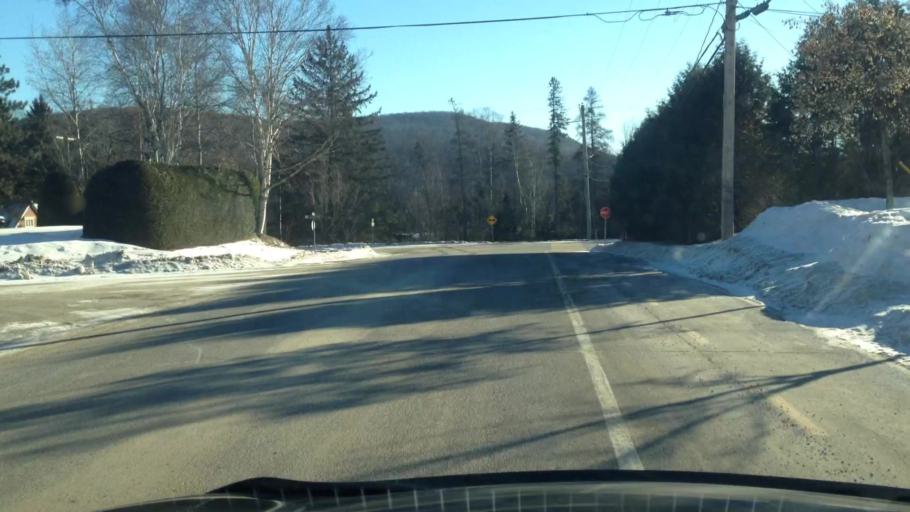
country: CA
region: Quebec
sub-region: Laurentides
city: Mont-Tremblant
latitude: 46.1224
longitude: -74.6064
